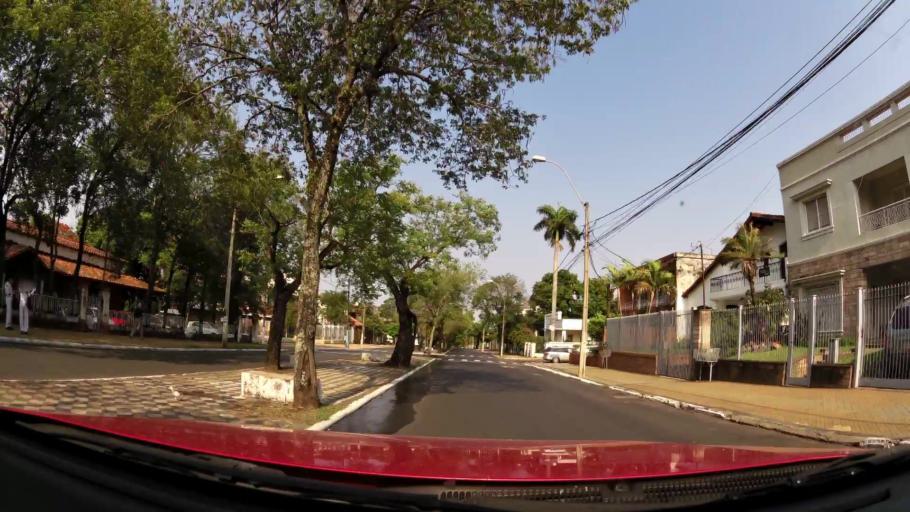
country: PY
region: Presidente Hayes
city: Nanawa
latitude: -25.2903
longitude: -57.6635
